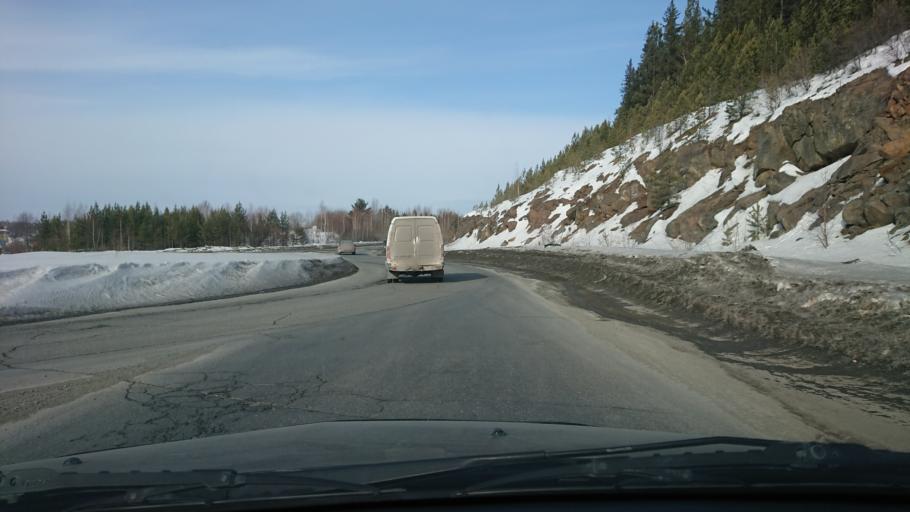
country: RU
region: Sverdlovsk
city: Revda
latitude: 56.7966
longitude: 59.9859
